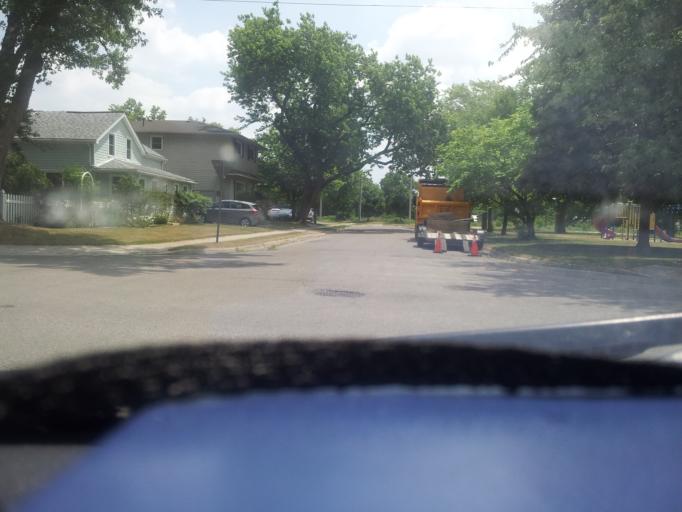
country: CA
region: Ontario
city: Stratford
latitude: 43.3617
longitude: -80.9943
